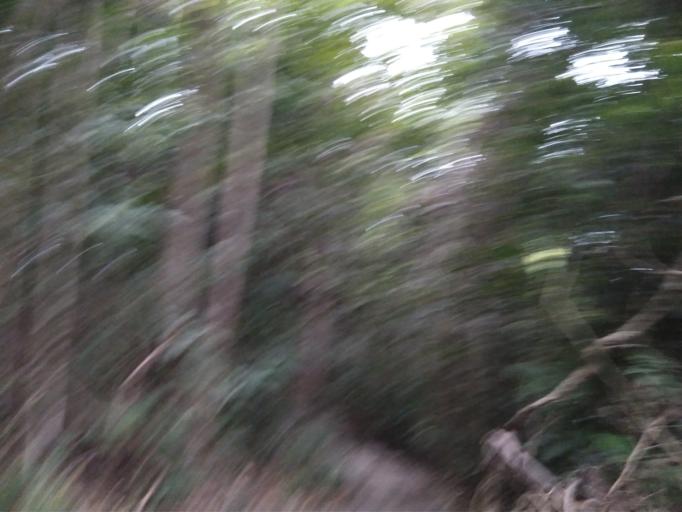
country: TH
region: Krabi
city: Ko Lanta
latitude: 7.4706
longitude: 99.1019
